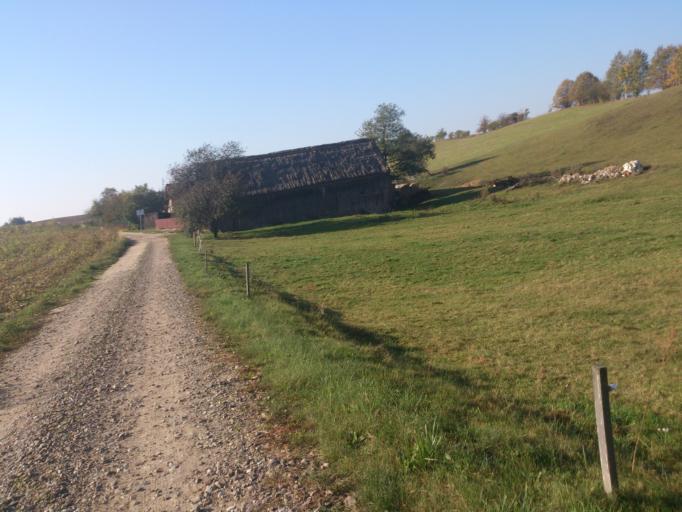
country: PL
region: Kujawsko-Pomorskie
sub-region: Powiat brodnicki
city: Gorzno
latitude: 53.2117
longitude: 19.6630
